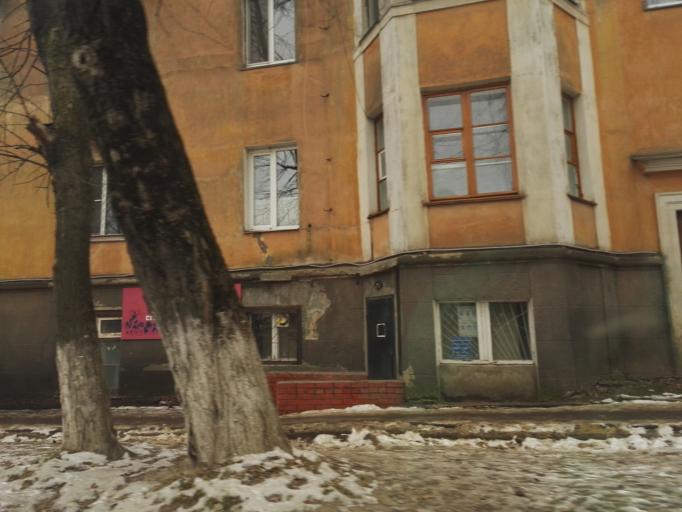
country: RU
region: Tula
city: Tula
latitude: 54.1759
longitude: 37.6191
